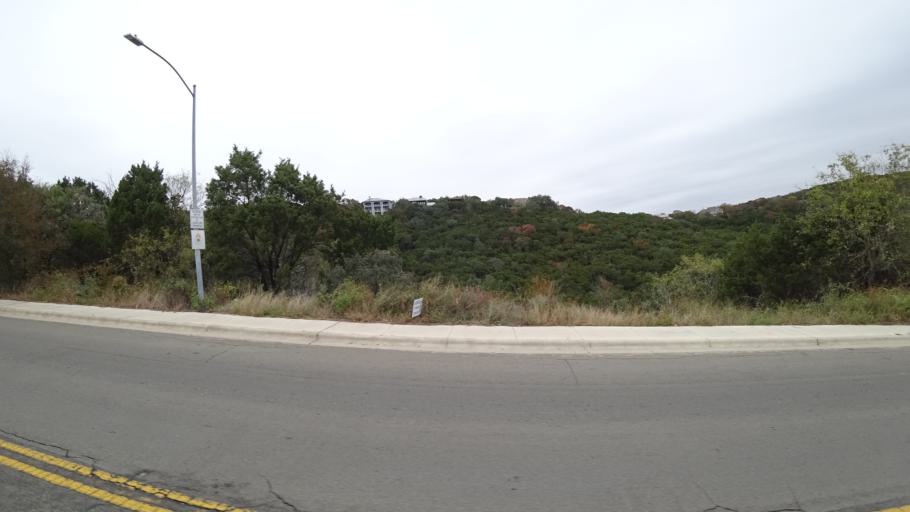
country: US
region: Texas
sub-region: Williamson County
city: Jollyville
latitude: 30.3726
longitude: -97.7989
